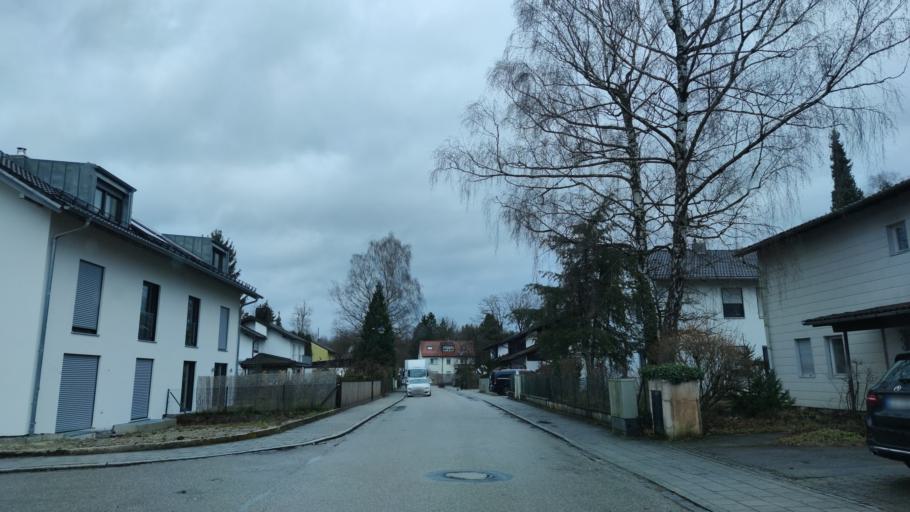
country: DE
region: Bavaria
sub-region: Upper Bavaria
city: Hohenbrunn
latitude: 48.0619
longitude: 11.6939
